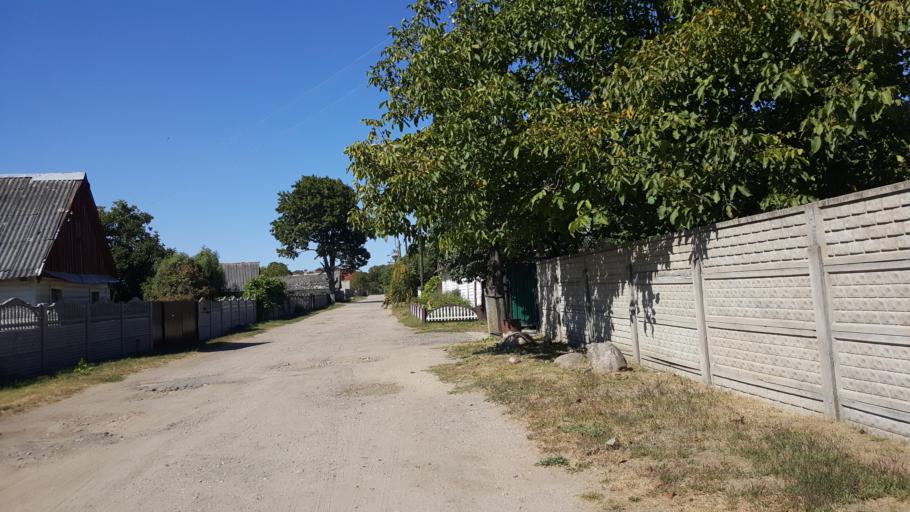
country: BY
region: Brest
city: Vysokaye
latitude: 52.2343
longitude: 23.4997
